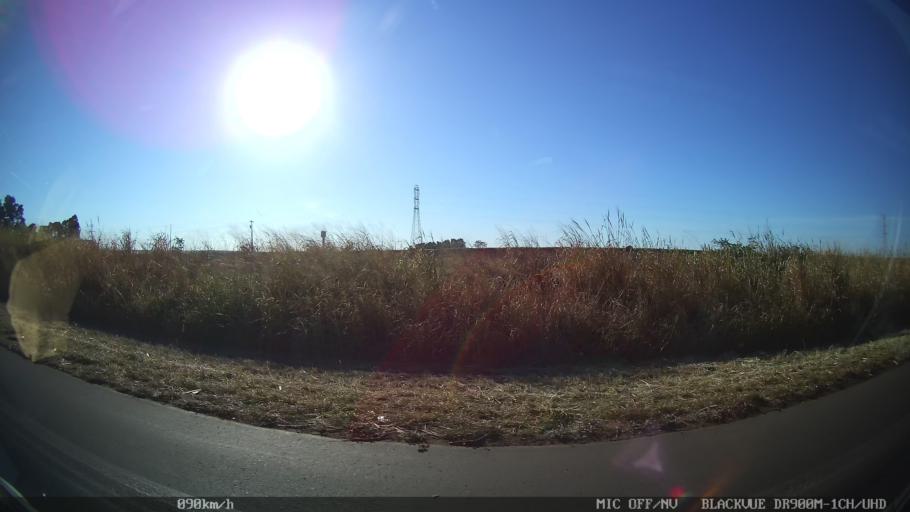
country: BR
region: Sao Paulo
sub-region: Olimpia
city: Olimpia
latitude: -20.6991
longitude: -48.9355
